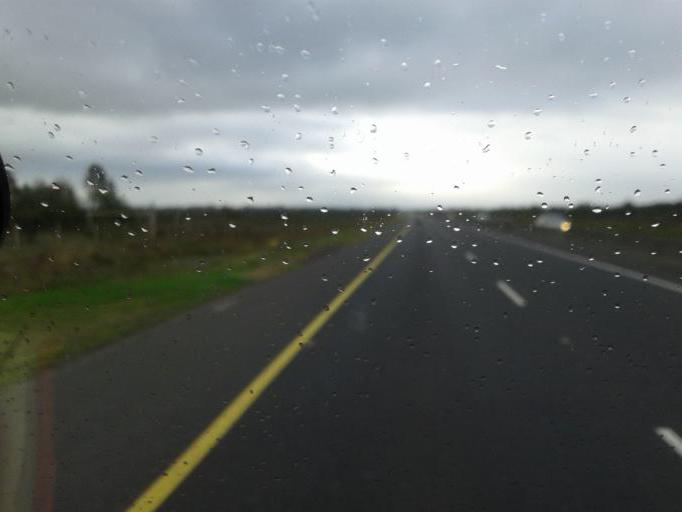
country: IE
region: Munster
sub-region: County Limerick
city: Castleconnell
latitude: 52.7229
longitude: -8.4679
